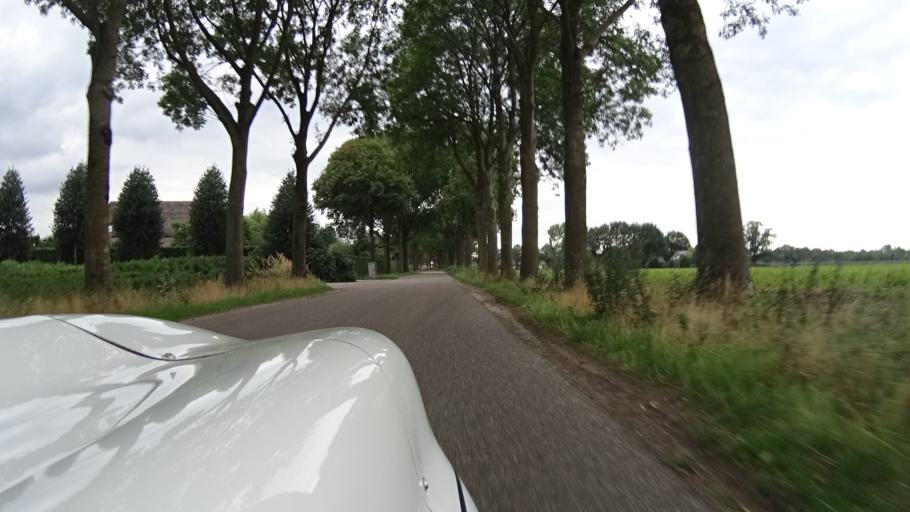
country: NL
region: North Brabant
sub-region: Gemeente Veghel
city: Erp
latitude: 51.6056
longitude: 5.6250
